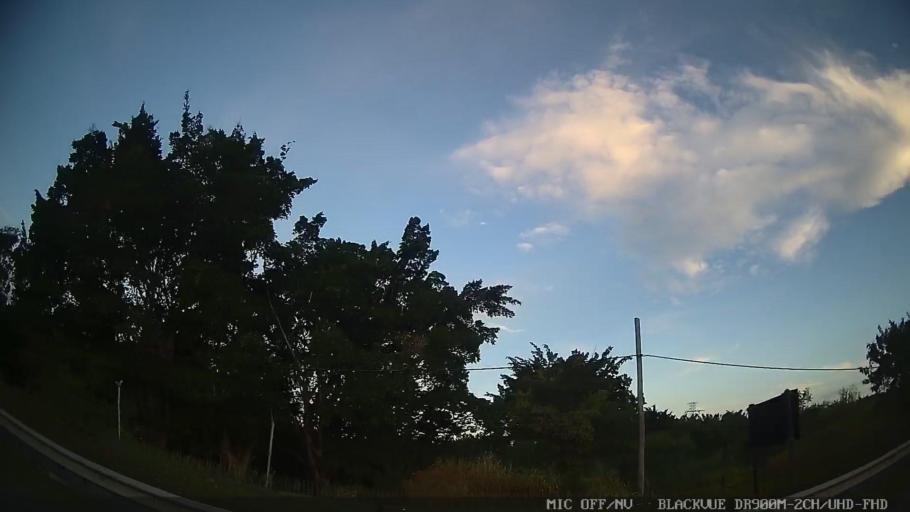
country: BR
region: Sao Paulo
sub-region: Indaiatuba
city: Indaiatuba
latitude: -23.1366
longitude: -47.2412
